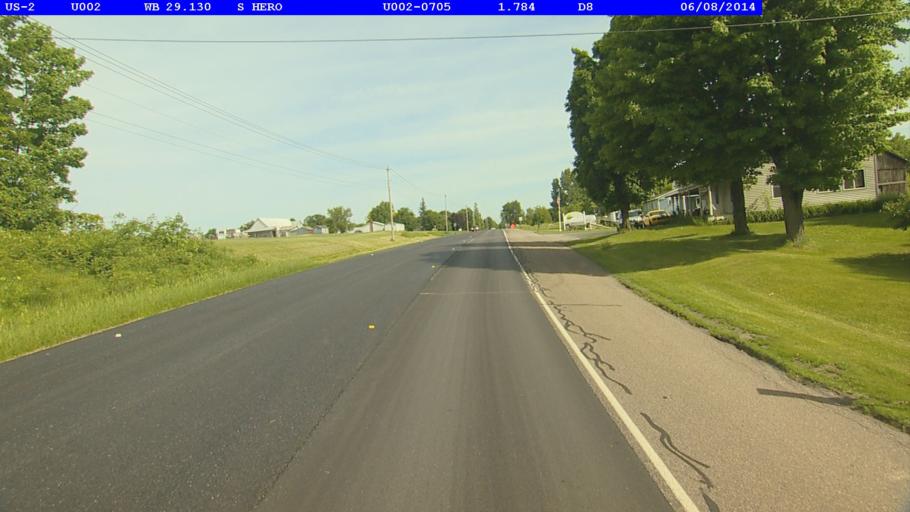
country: US
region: New York
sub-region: Clinton County
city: Cumberland Head
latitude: 44.6555
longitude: -73.3205
